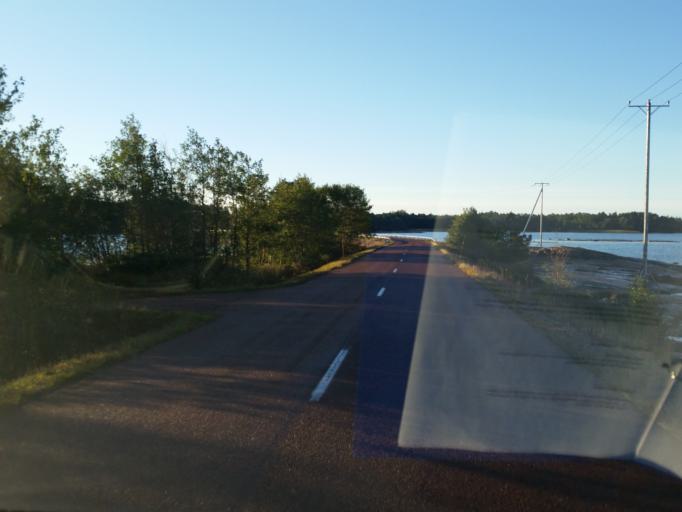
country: AX
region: Alands skaergard
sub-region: Vardoe
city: Vardoe
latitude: 60.3132
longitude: 20.3743
